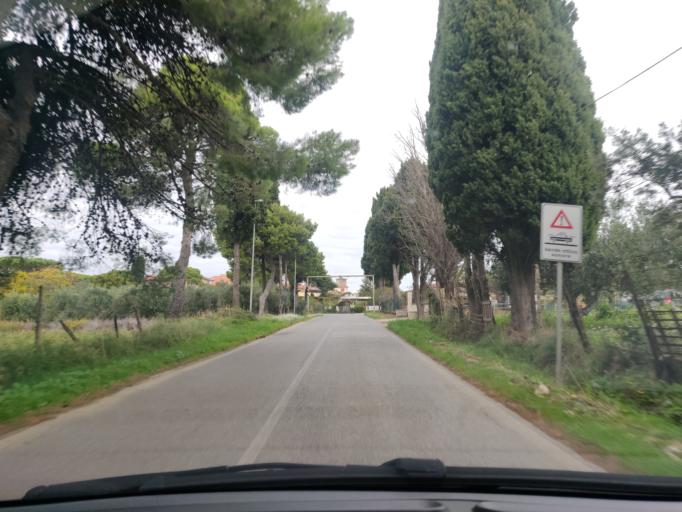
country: IT
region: Latium
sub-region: Citta metropolitana di Roma Capitale
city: Aurelia
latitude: 42.1357
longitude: 11.7883
